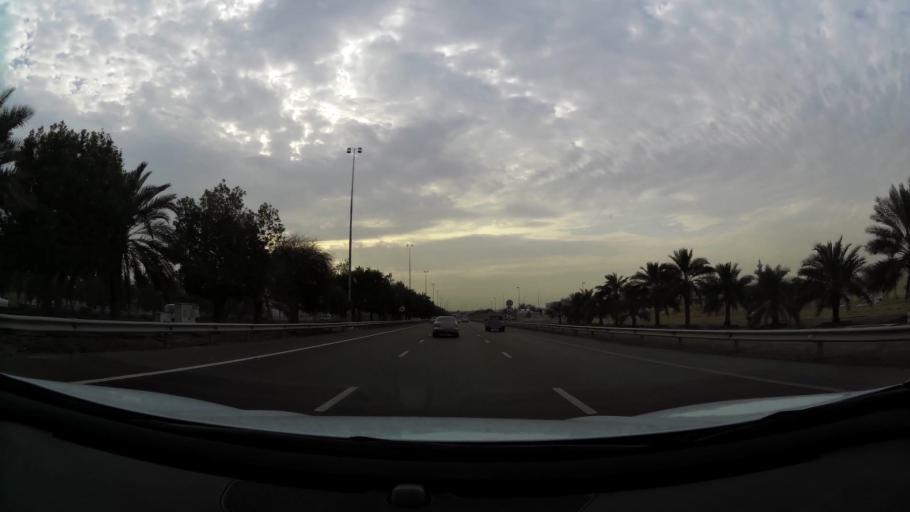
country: AE
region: Abu Dhabi
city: Abu Dhabi
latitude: 24.2881
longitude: 54.6385
